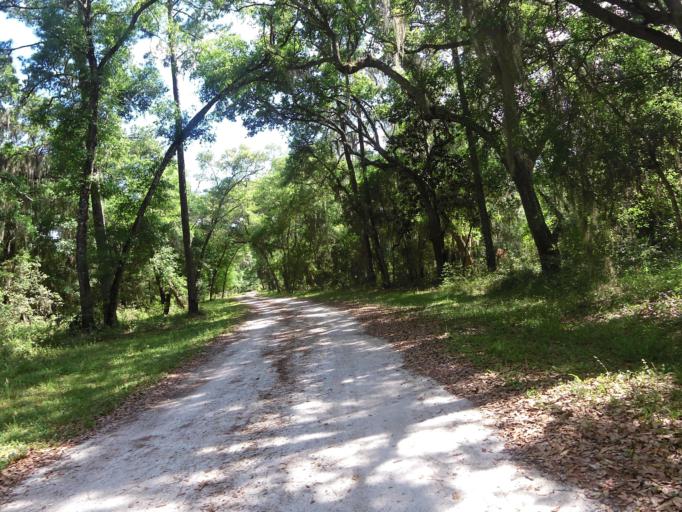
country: US
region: Florida
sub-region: Saint Johns County
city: Palm Valley
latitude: 30.1315
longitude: -81.3675
